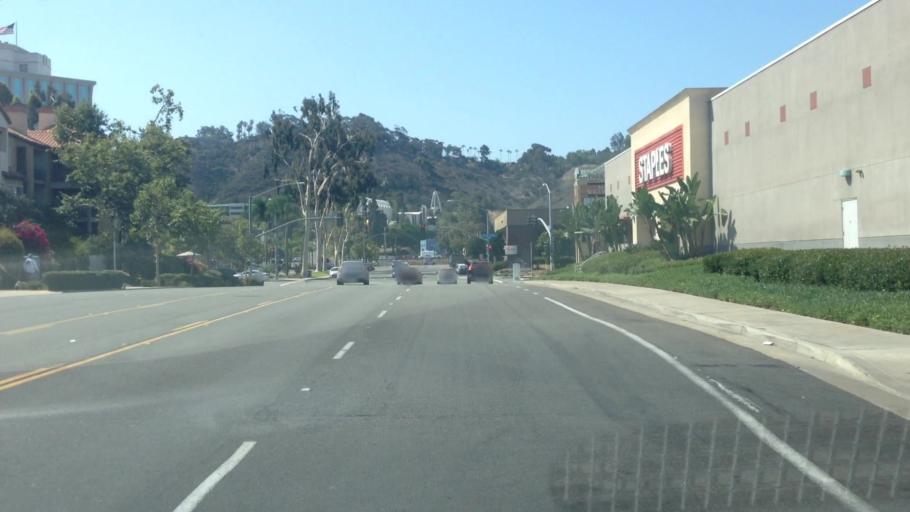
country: US
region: California
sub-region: San Diego County
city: San Diego
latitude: 32.7719
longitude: -117.1446
